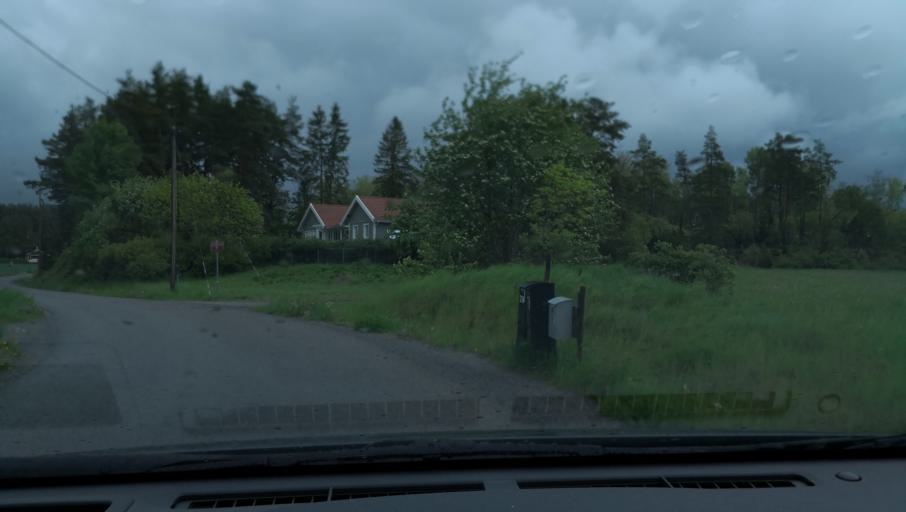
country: SE
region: Uppsala
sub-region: Enkopings Kommun
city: Orsundsbro
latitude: 59.8077
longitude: 17.3806
